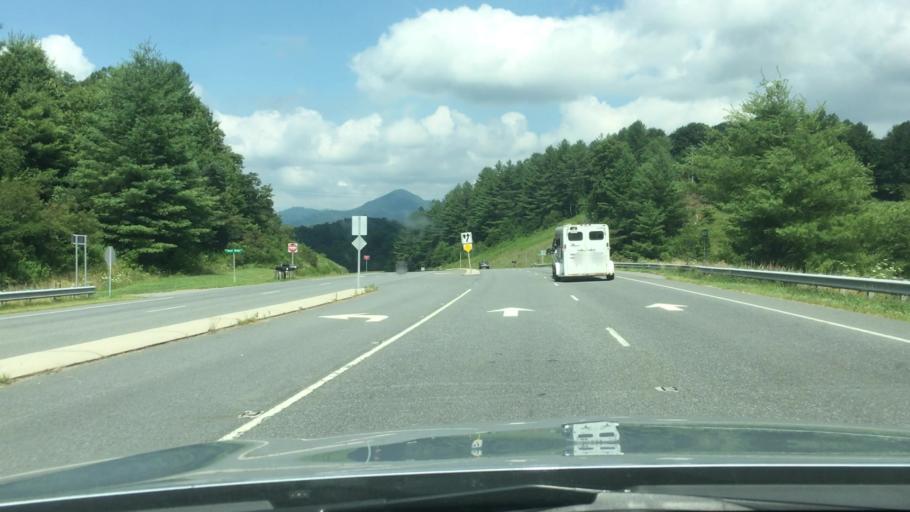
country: US
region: North Carolina
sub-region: Yancey County
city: Burnsville
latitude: 35.9124
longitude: -82.3913
